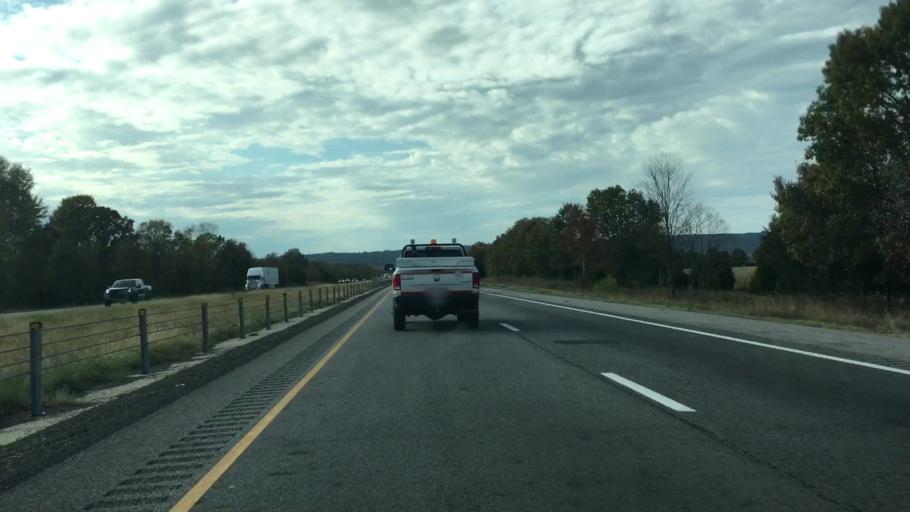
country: US
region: Arkansas
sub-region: Pope County
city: Atkins
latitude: 35.2485
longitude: -92.8762
